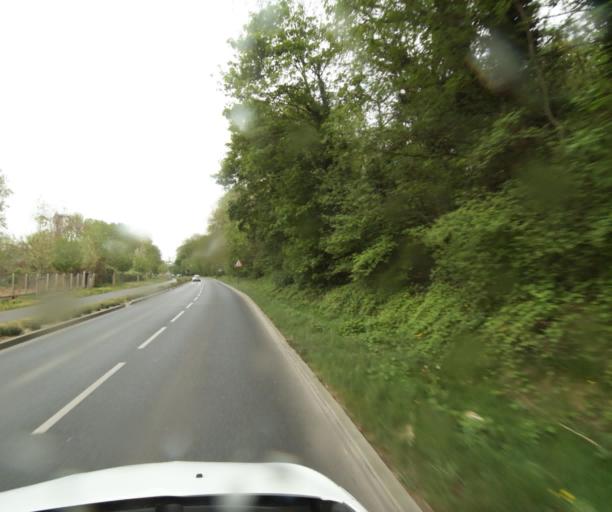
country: FR
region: Ile-de-France
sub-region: Departement de Seine-et-Marne
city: Noisiel
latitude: 48.8558
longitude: 2.6352
